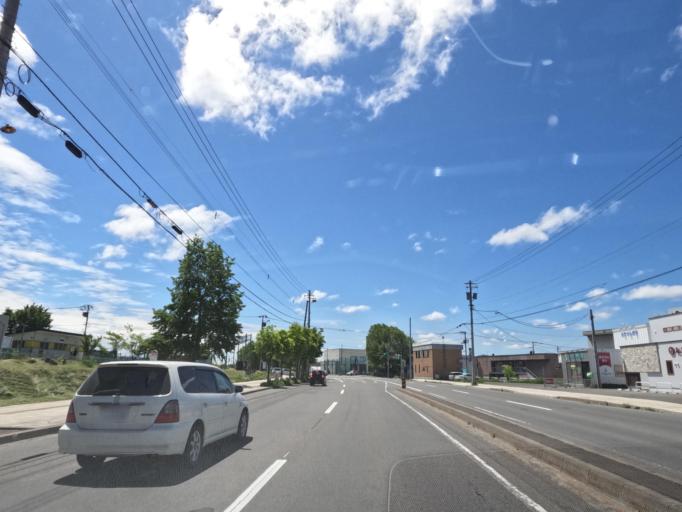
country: JP
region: Hokkaido
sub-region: Asahikawa-shi
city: Asahikawa
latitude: 43.7455
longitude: 142.3579
